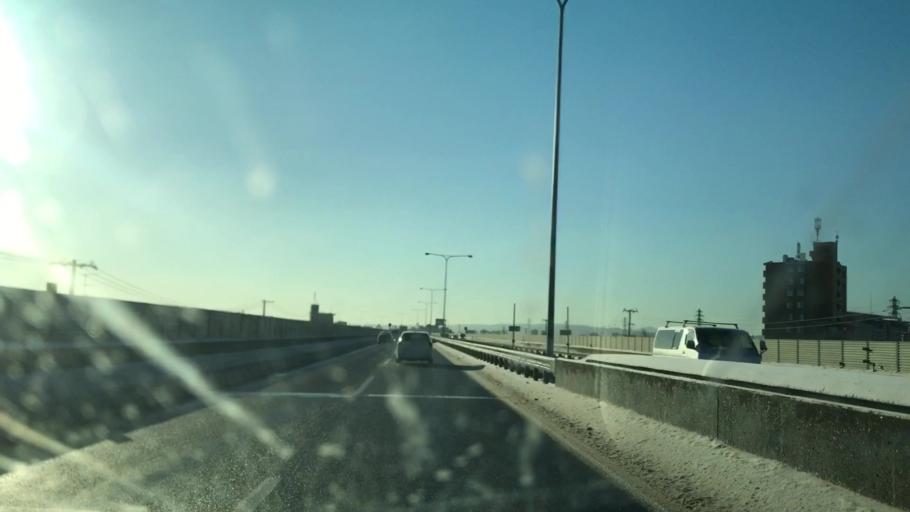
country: JP
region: Hokkaido
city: Sapporo
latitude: 43.0642
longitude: 141.4236
